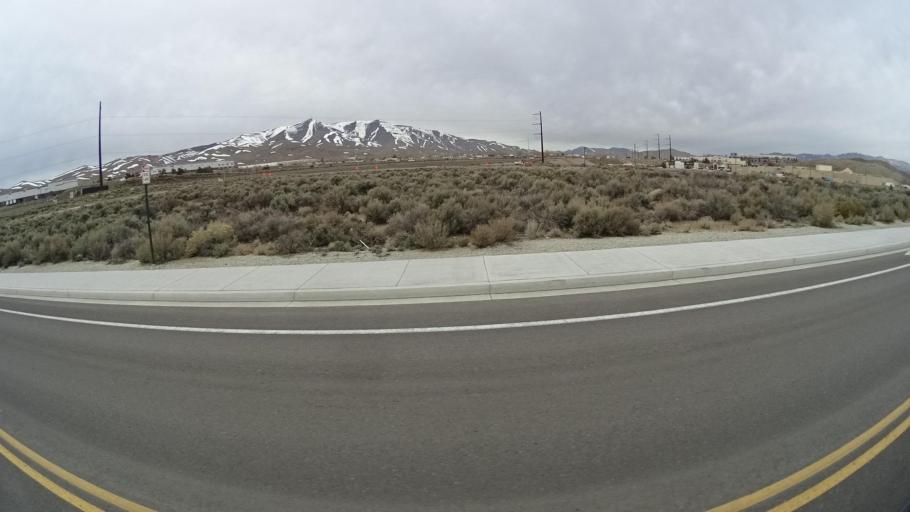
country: US
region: Nevada
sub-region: Washoe County
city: Golden Valley
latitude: 39.6098
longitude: -119.8448
